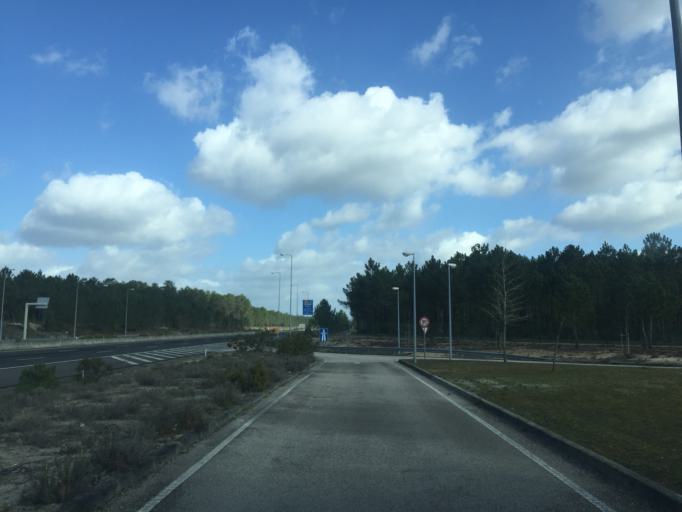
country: PT
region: Leiria
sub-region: Alcobaca
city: Pataias
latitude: 39.6208
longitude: -8.9899
